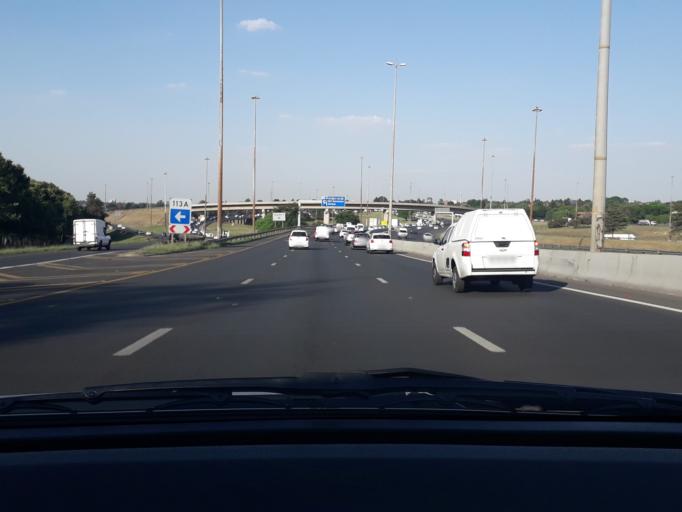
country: ZA
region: Gauteng
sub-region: Ekurhuleni Metropolitan Municipality
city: Germiston
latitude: -26.1721
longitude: 28.1285
